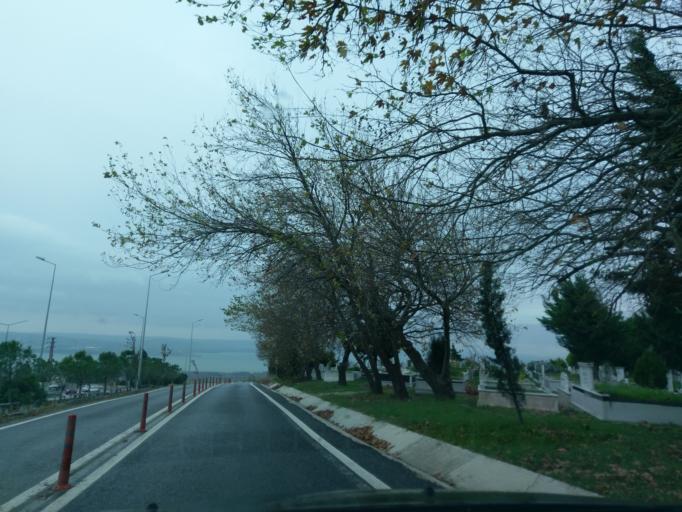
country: TR
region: Istanbul
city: Bueyuekcekmece
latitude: 41.0267
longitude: 28.6114
